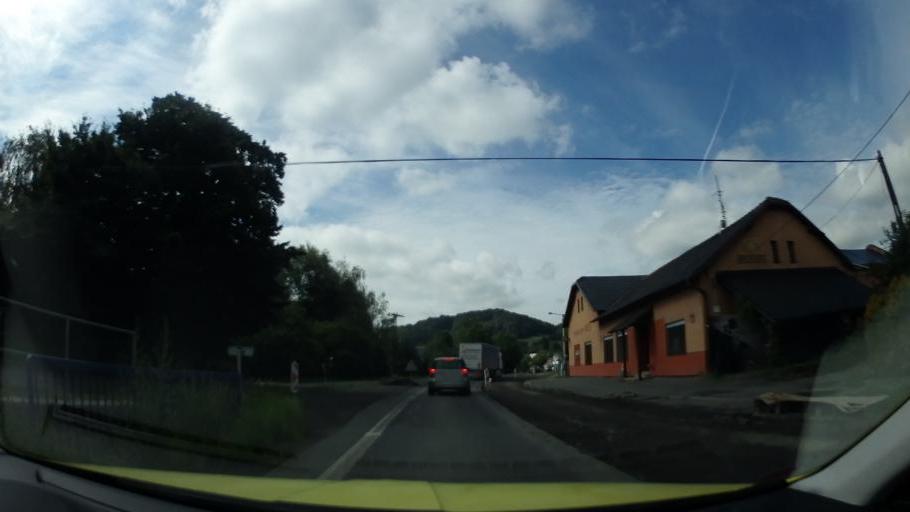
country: CZ
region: Moravskoslezsky
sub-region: Okres Novy Jicin
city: Novy Jicin
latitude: 49.5772
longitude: 18.0225
